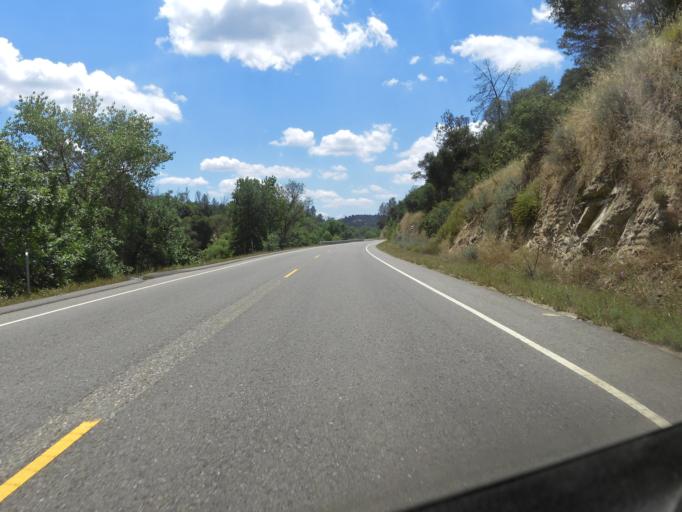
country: US
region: California
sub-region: Madera County
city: Coarsegold
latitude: 37.1741
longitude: -119.6332
